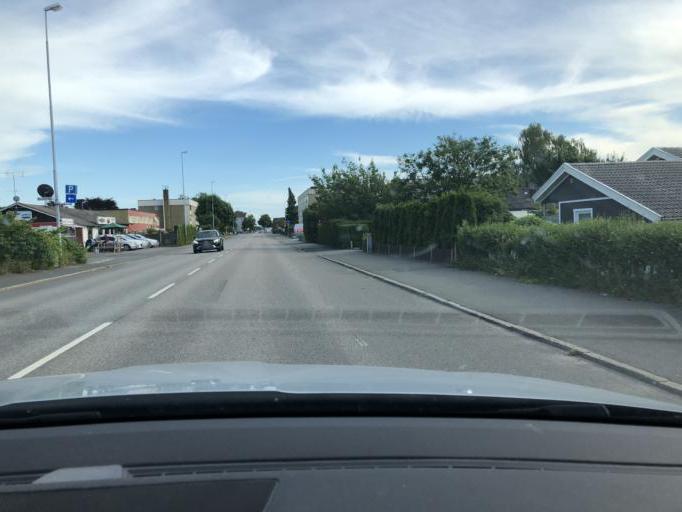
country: SE
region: Skane
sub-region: Bromolla Kommun
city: Bromoella
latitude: 56.0717
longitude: 14.4769
